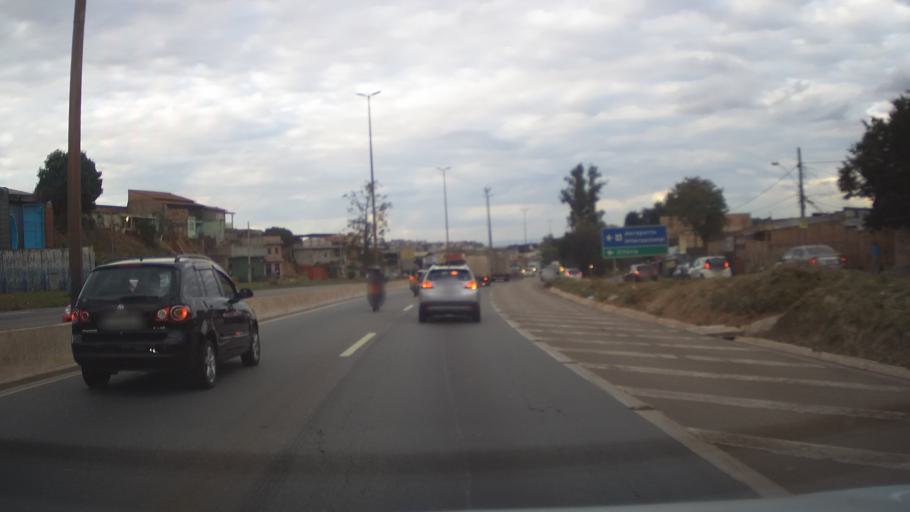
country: BR
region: Minas Gerais
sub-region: Contagem
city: Contagem
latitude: -19.9242
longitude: -44.0050
